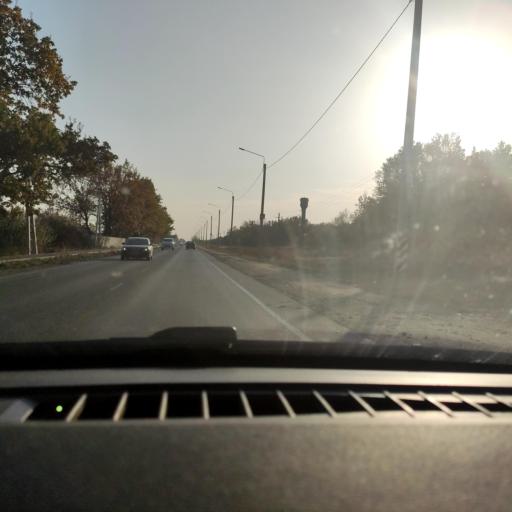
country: RU
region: Voronezj
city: Semiluki
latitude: 51.7328
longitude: 39.0407
